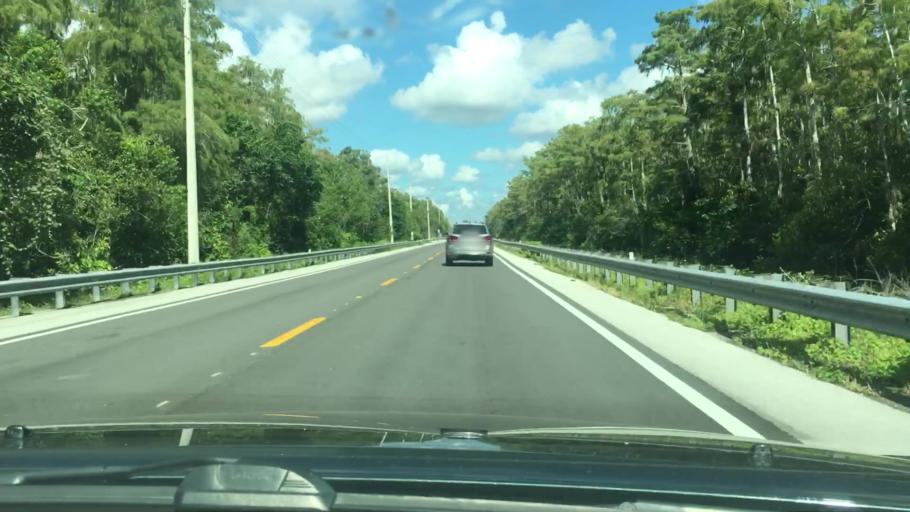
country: US
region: Florida
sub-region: Miami-Dade County
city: Kendall West
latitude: 25.8007
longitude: -80.8681
